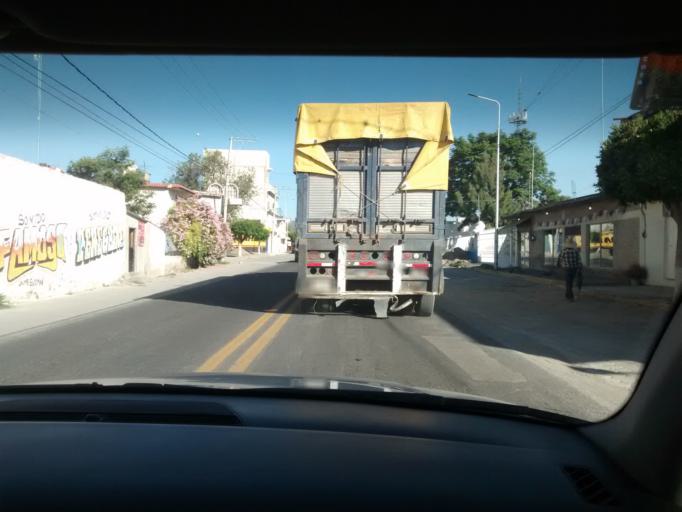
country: MX
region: Puebla
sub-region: Tepanco de Lopez
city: San Andres Cacaloapan
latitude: 18.5555
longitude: -97.5614
